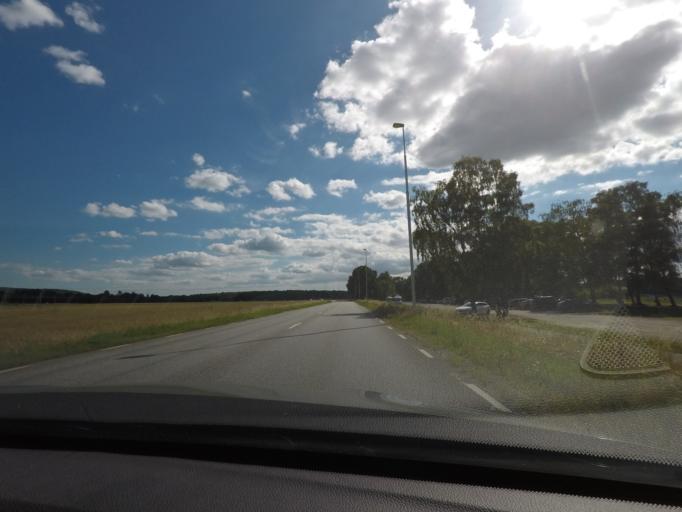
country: SE
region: Skane
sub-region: Hassleholms Kommun
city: Tormestorp
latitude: 56.1213
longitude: 13.7364
